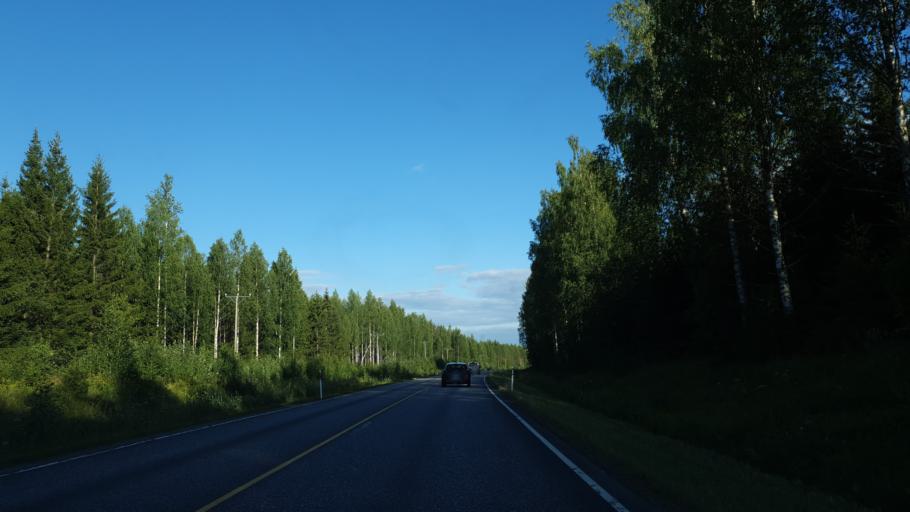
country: FI
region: North Karelia
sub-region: Joensuu
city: Outokumpu
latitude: 62.5304
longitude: 28.9829
